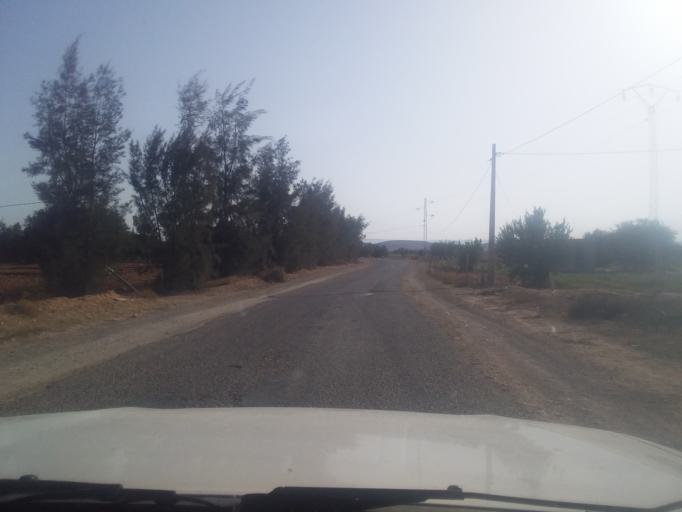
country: TN
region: Qabis
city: Matmata
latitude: 33.5890
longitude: 10.2778
